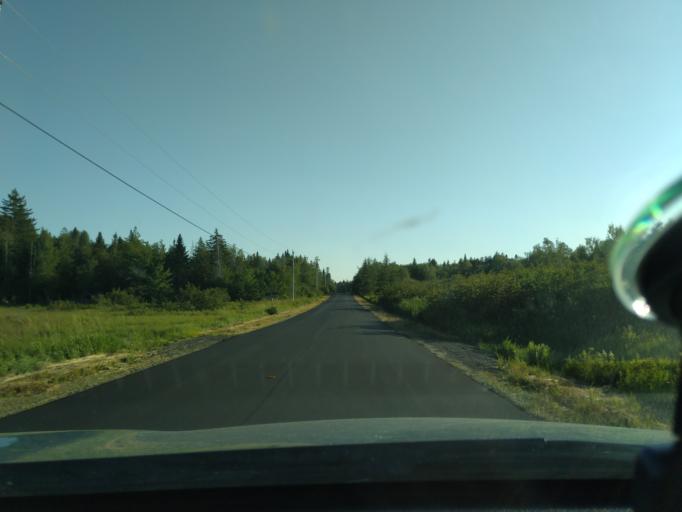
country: US
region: Maine
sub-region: Washington County
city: East Machias
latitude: 44.6976
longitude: -67.1595
